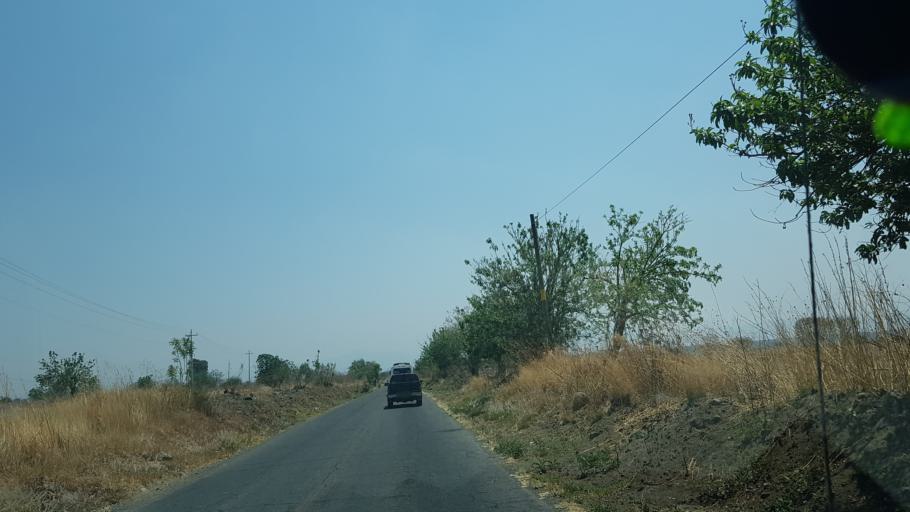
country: MX
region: Puebla
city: Tochimilco
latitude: 18.8881
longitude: -98.5363
